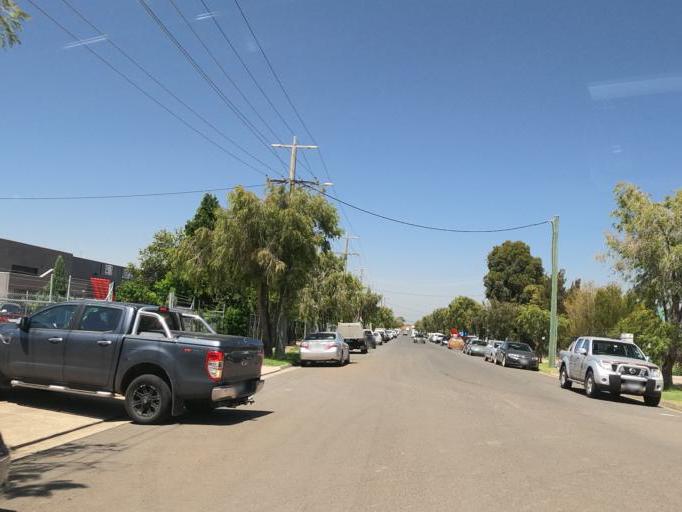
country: AU
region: Victoria
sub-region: Whittlesea
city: Epping
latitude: -37.6448
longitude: 145.0126
